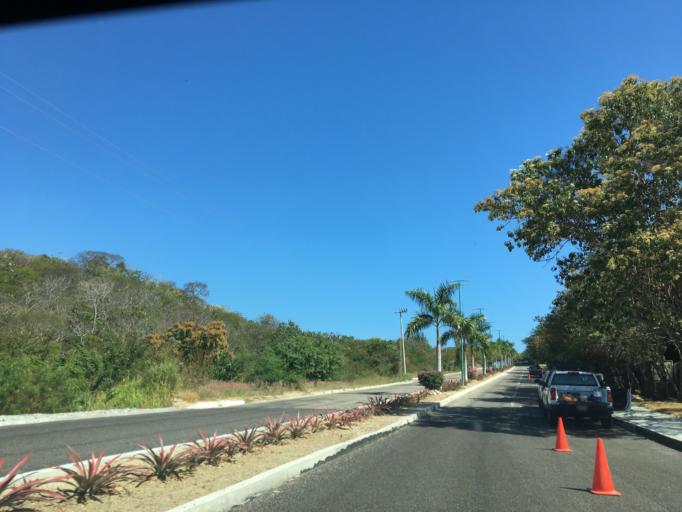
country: MX
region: Oaxaca
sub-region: Santa Maria Huatulco
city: Crucecita
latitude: 15.7839
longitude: -96.0640
